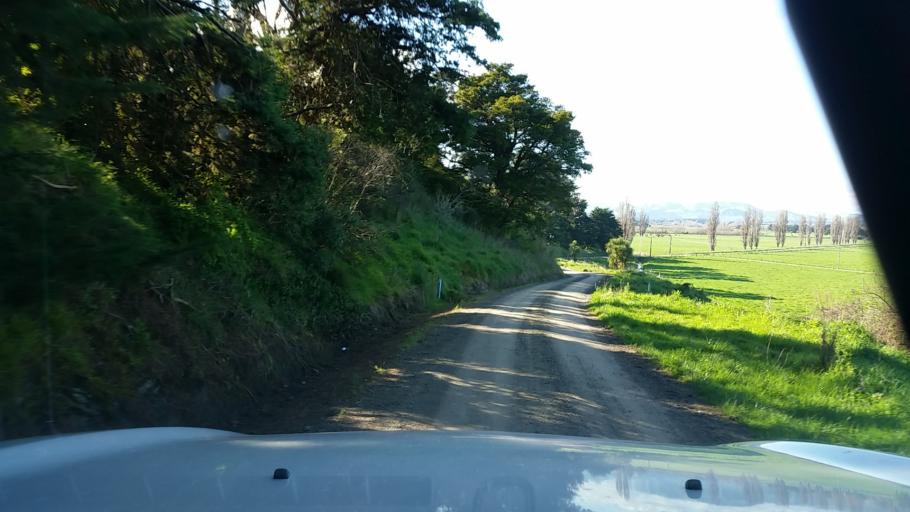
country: NZ
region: Wellington
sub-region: South Wairarapa District
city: Waipawa
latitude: -41.2087
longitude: 175.3851
